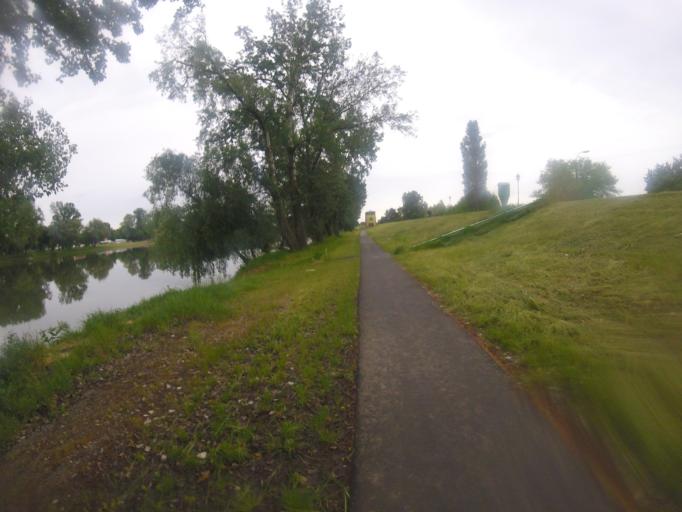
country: HU
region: Borsod-Abauj-Zemplen
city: Tokaj
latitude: 48.1164
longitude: 21.4145
